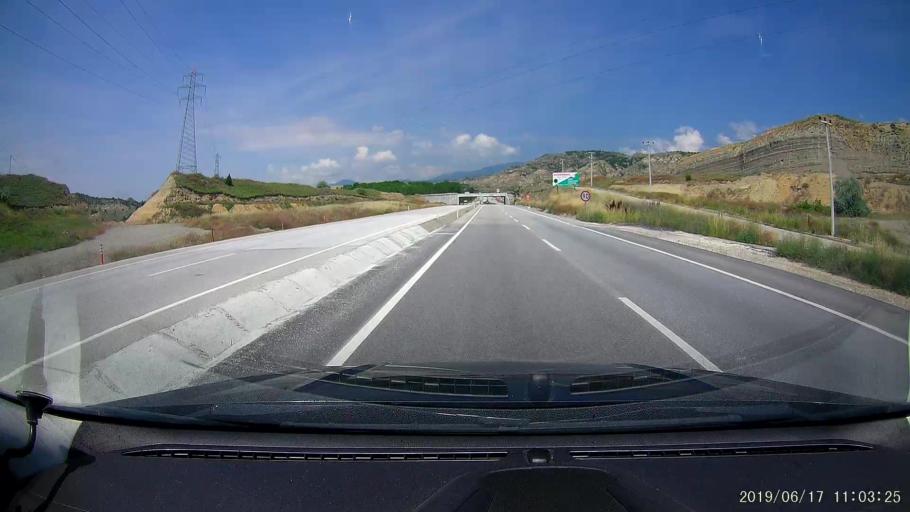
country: TR
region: Kastamonu
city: Tosya
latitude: 41.0176
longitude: 34.1158
